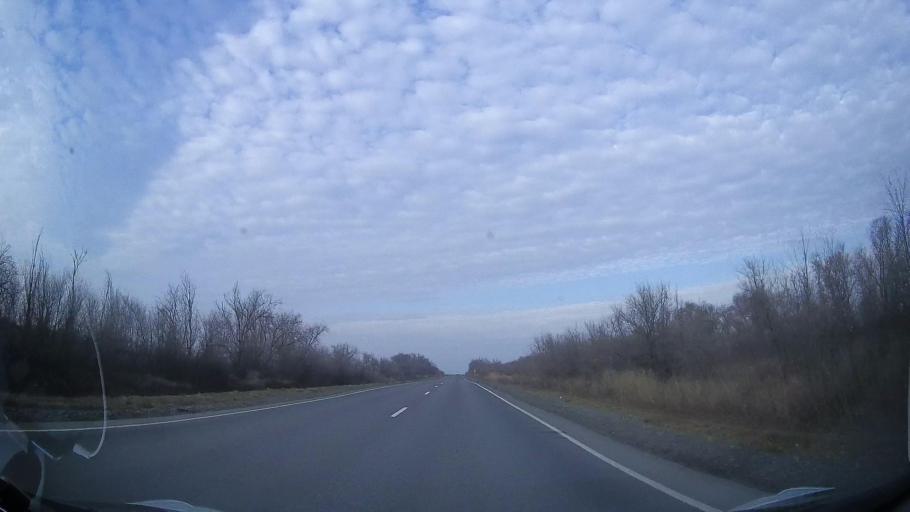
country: RU
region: Rostov
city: Bagayevskaya
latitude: 47.1418
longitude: 40.2766
